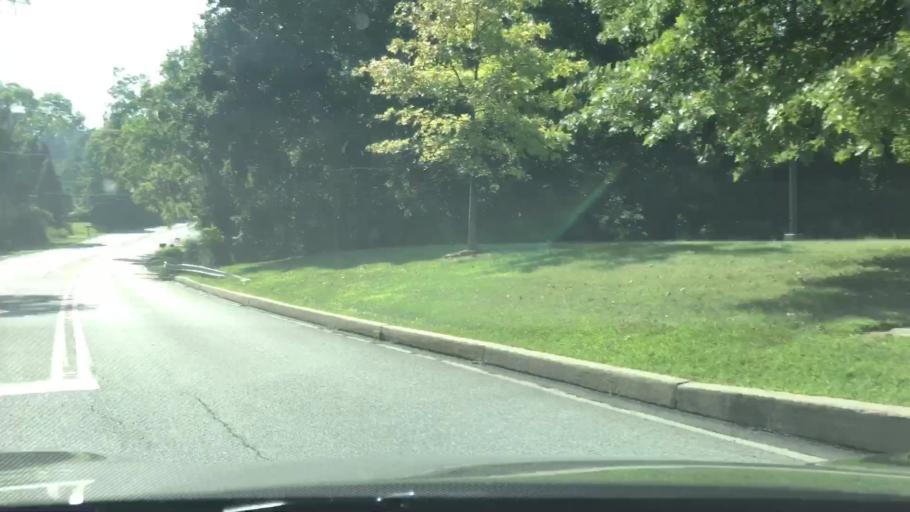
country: US
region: Pennsylvania
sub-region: Montgomery County
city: Dresher
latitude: 40.1551
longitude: -75.1752
